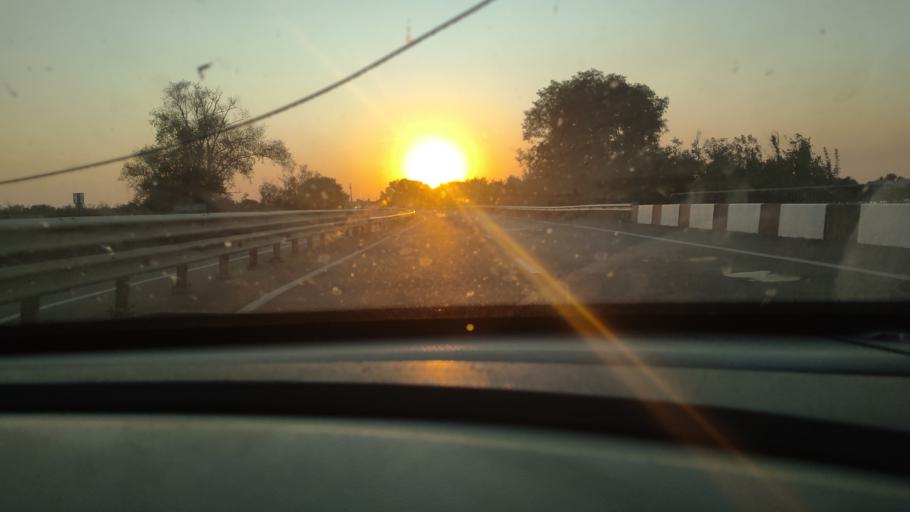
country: RU
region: Krasnodarskiy
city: Timashevsk
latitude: 45.5998
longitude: 38.9401
